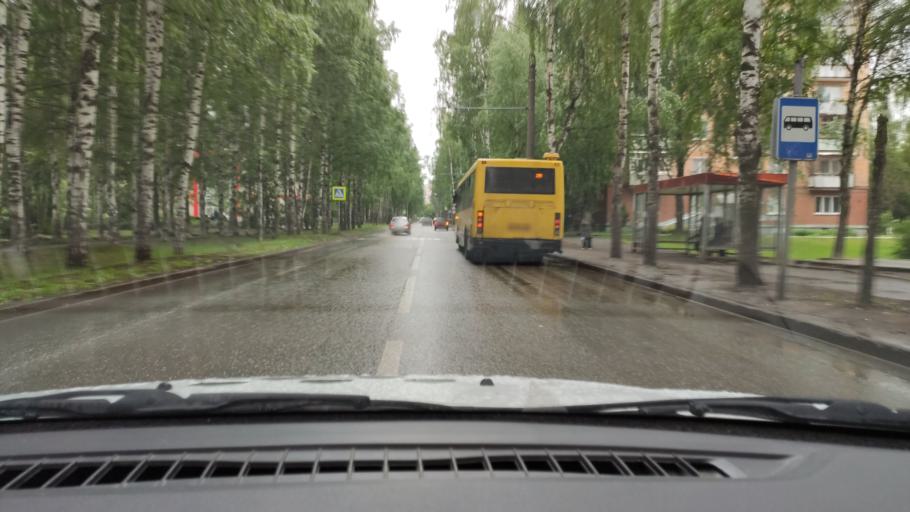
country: RU
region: Udmurtiya
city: Izhevsk
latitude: 56.8814
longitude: 53.1863
